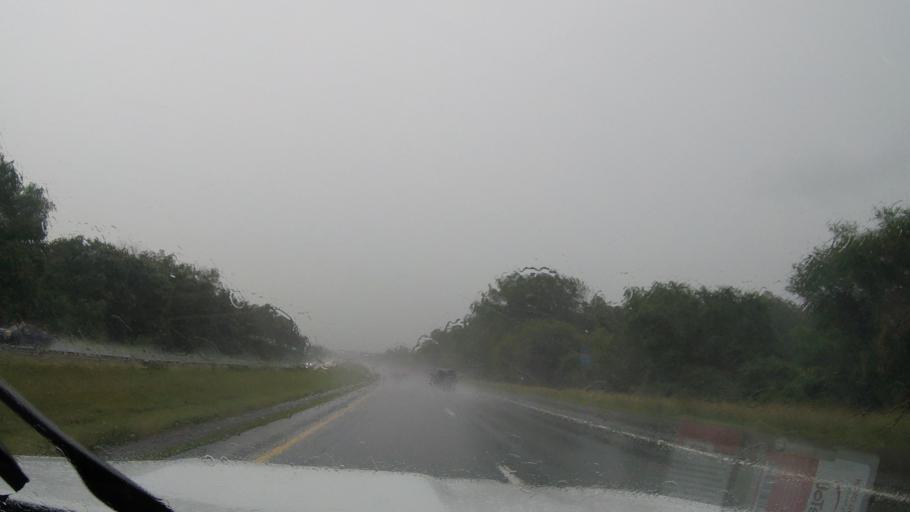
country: US
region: New York
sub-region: Seneca County
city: Waterloo
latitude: 42.9679
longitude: -76.8385
